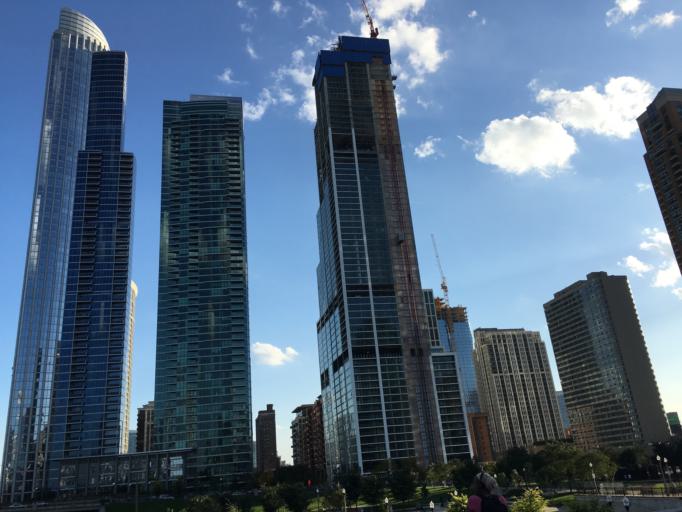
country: US
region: Illinois
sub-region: Cook County
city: Chicago
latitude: 41.8693
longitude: -87.6221
